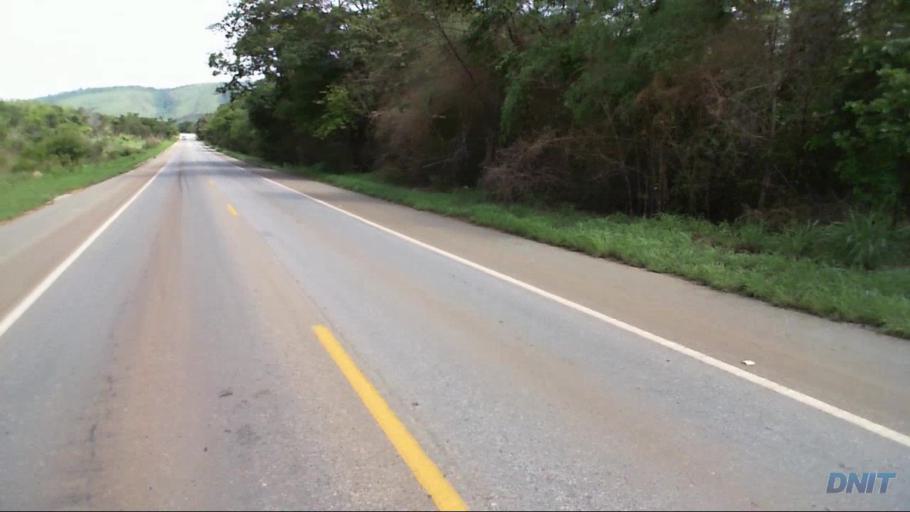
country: BR
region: Goias
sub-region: Barro Alto
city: Barro Alto
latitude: -15.1647
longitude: -48.7989
